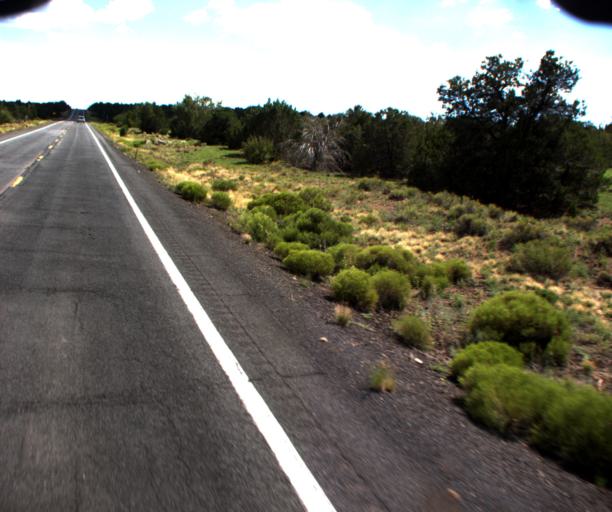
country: US
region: Arizona
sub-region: Coconino County
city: Williams
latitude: 35.4412
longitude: -112.1716
